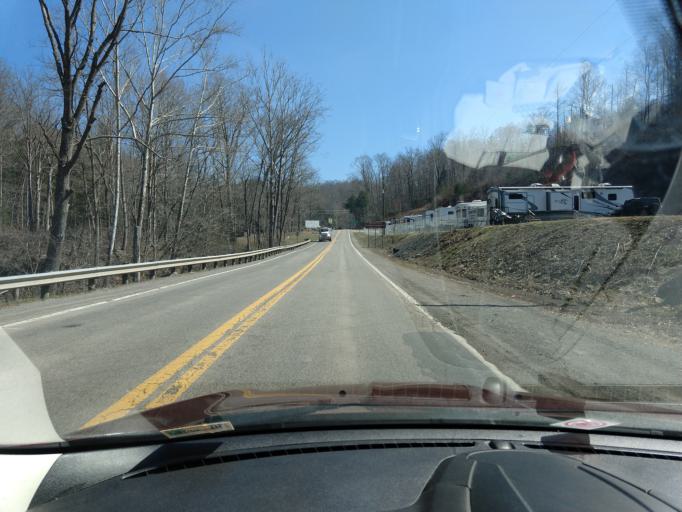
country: US
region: West Virginia
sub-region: Braxton County
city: Sutton
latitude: 38.6891
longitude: -80.6783
